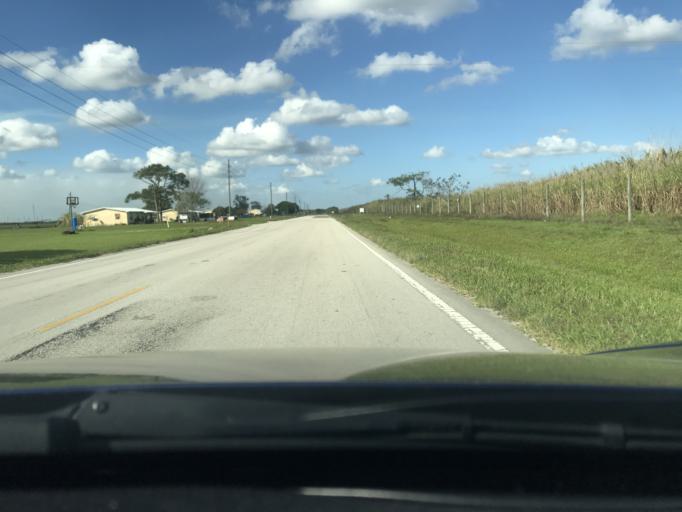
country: US
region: Florida
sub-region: Okeechobee County
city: Taylor Creek
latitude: 27.2668
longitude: -80.6946
